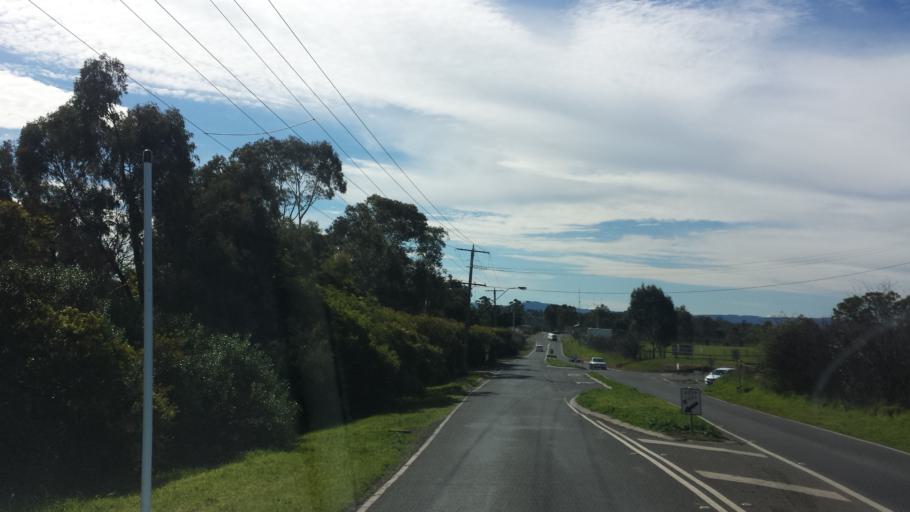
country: AU
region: Victoria
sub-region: Nillumbik
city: Research
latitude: -37.6888
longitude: 145.2161
